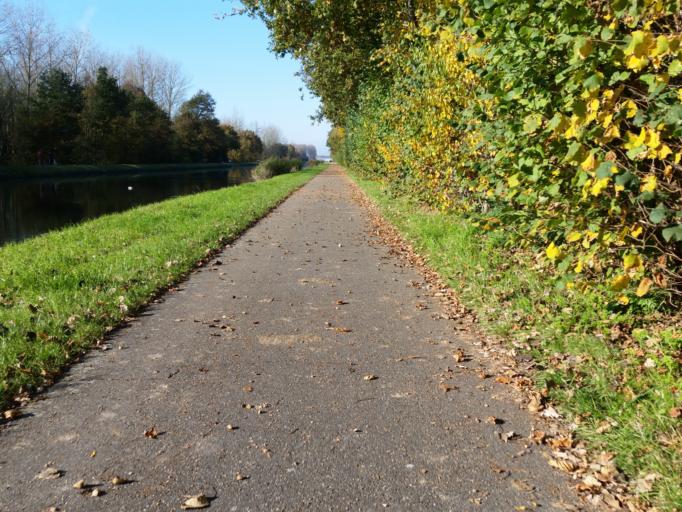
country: BE
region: Flanders
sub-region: Provincie Vlaams-Brabant
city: Herent
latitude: 50.9318
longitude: 4.6778
